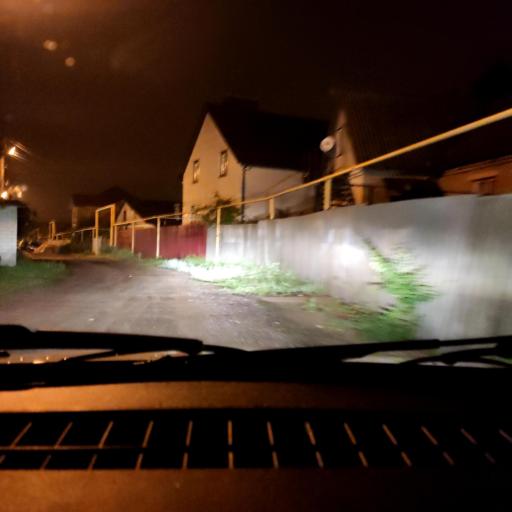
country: RU
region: Voronezj
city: Podgornoye
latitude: 51.7326
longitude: 39.1648
